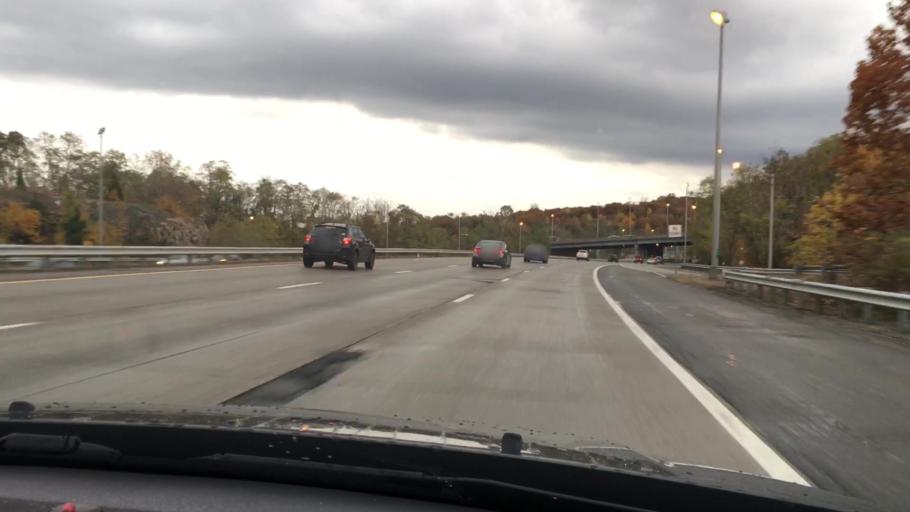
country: US
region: New Jersey
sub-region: Morris County
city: Riverdale
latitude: 40.9913
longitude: -74.3090
